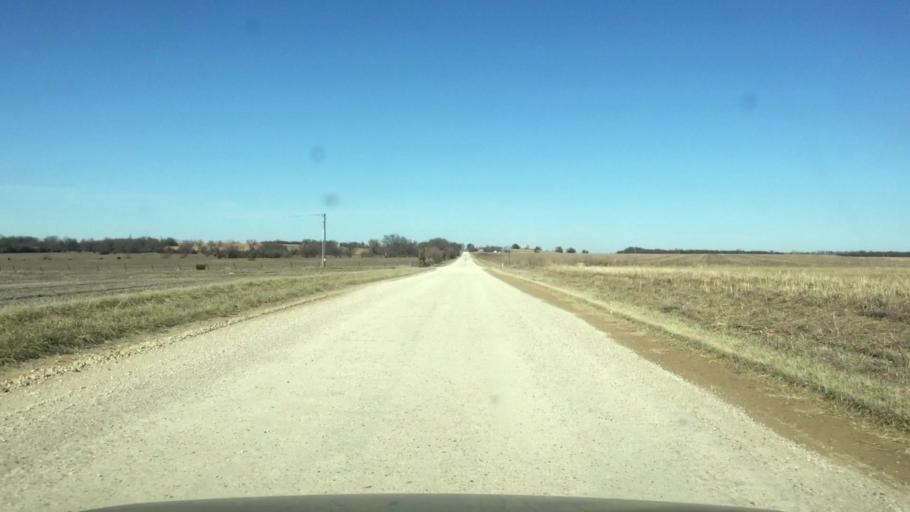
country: US
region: Kansas
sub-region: Allen County
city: Iola
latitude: 37.8626
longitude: -95.3910
